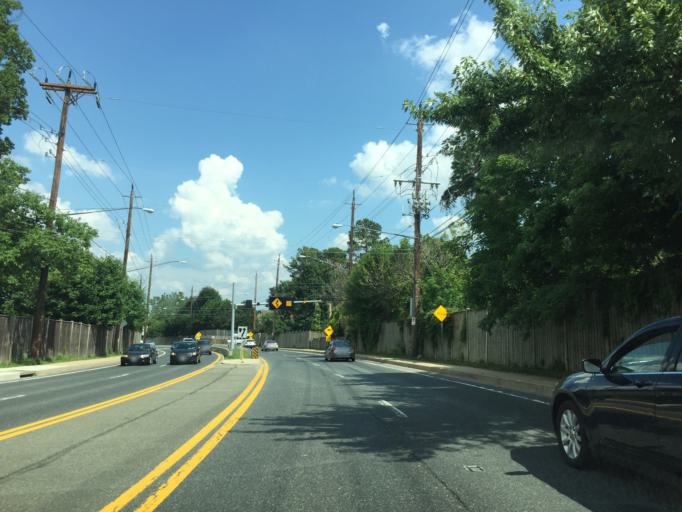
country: US
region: Maryland
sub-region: Montgomery County
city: Colesville
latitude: 39.0668
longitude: -76.9844
